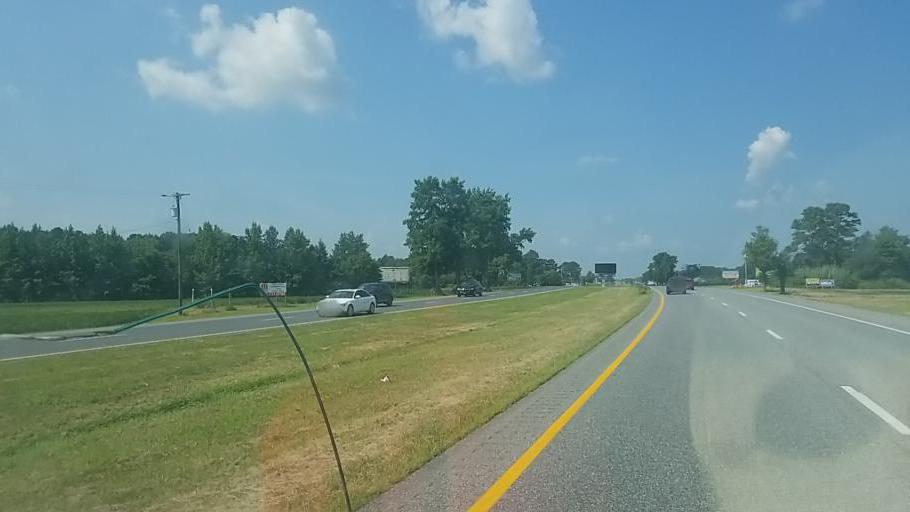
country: US
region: Maryland
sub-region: Worcester County
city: Berlin
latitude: 38.3472
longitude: -75.1774
